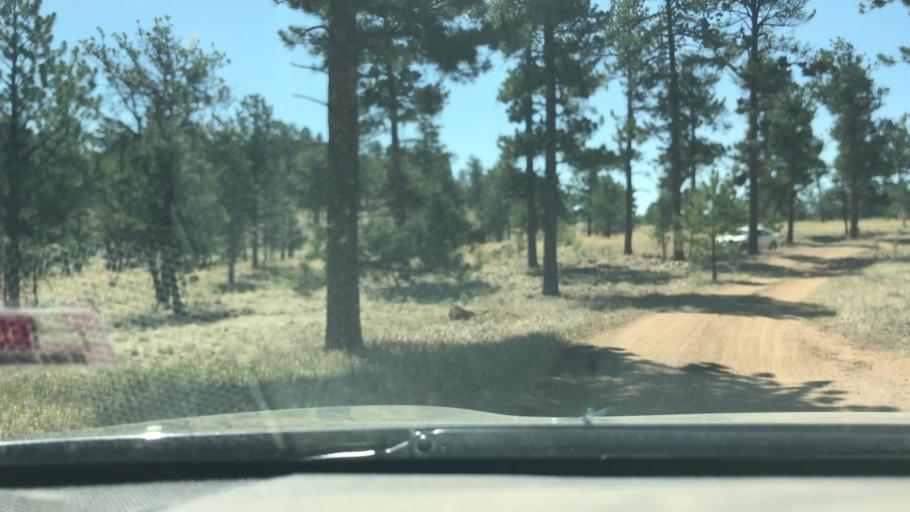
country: US
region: Colorado
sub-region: Teller County
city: Woodland Park
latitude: 38.9970
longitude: -105.3419
